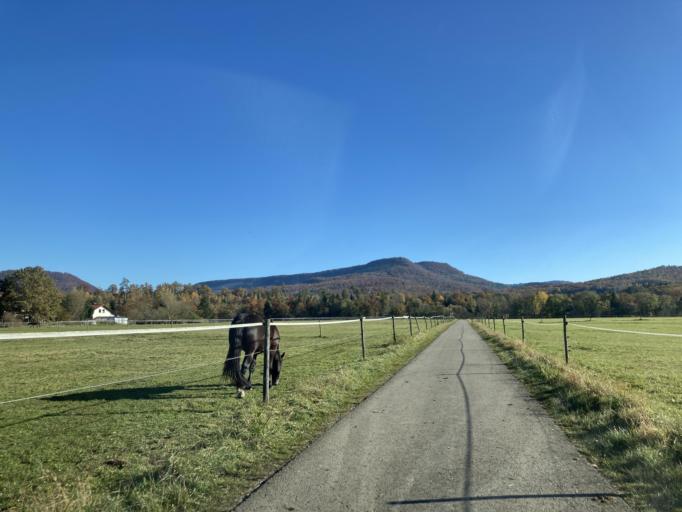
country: DE
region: Baden-Wuerttemberg
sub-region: Tuebingen Region
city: Ofterdingen
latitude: 48.3930
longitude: 9.0118
